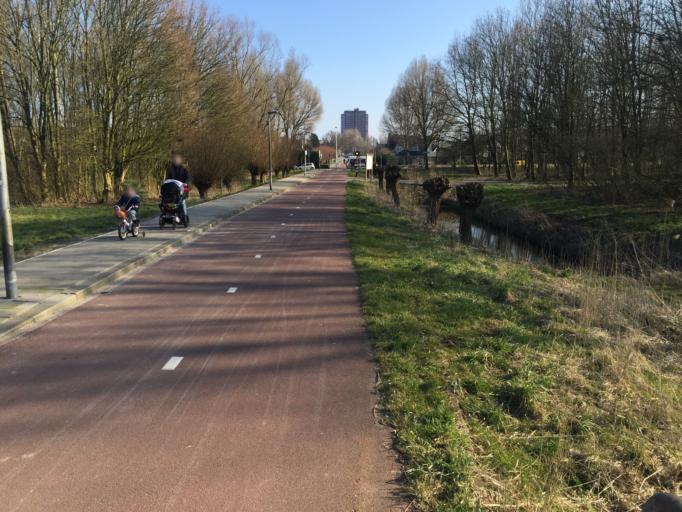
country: NL
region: South Holland
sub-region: Gemeente Capelle aan den IJssel
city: Capelle aan den IJssel
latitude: 51.9501
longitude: 4.5961
